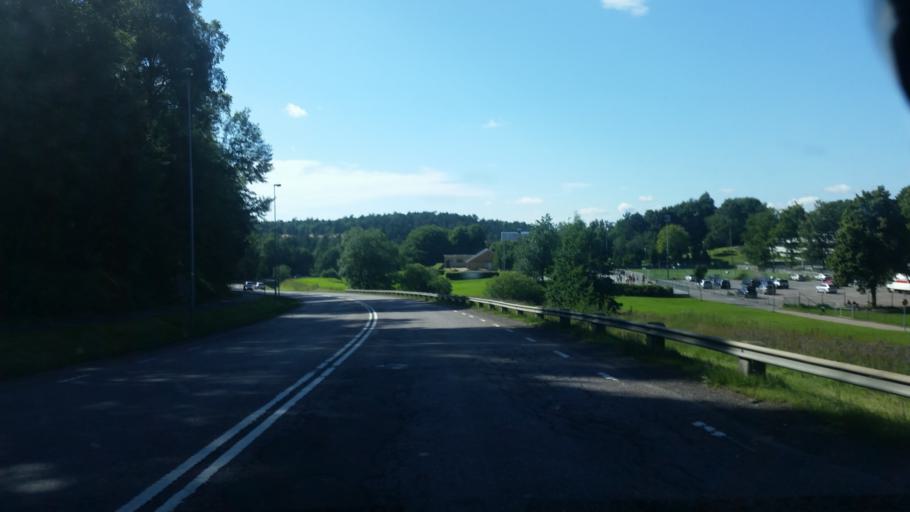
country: SE
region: Vaestra Goetaland
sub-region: Partille Kommun
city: Partille
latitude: 57.7274
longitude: 12.1172
